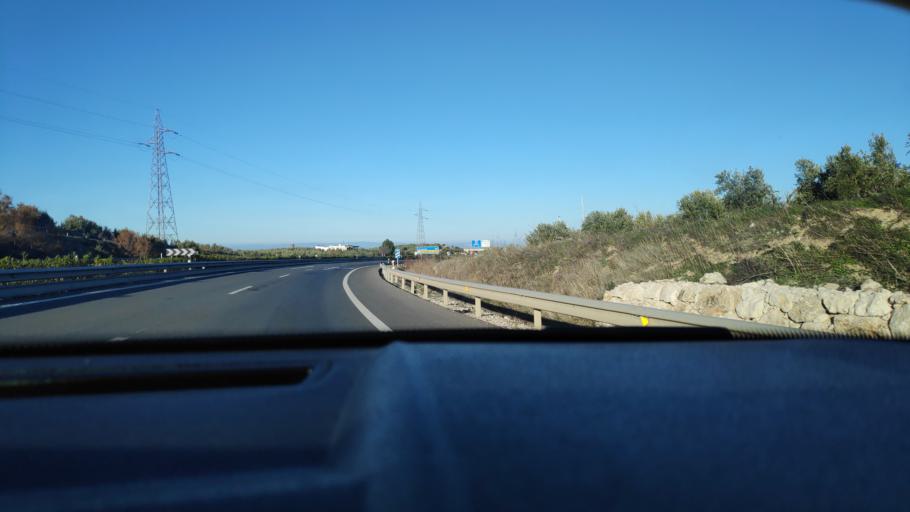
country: ES
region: Andalusia
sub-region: Provincia de Jaen
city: Torre del Campo
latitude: 37.7721
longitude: -3.9074
